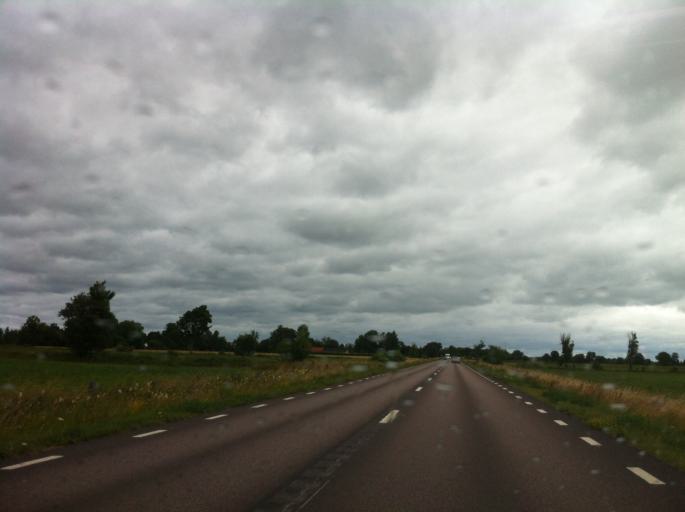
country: SE
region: Kalmar
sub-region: Borgholms Kommun
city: Borgholm
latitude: 57.1251
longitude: 16.9691
